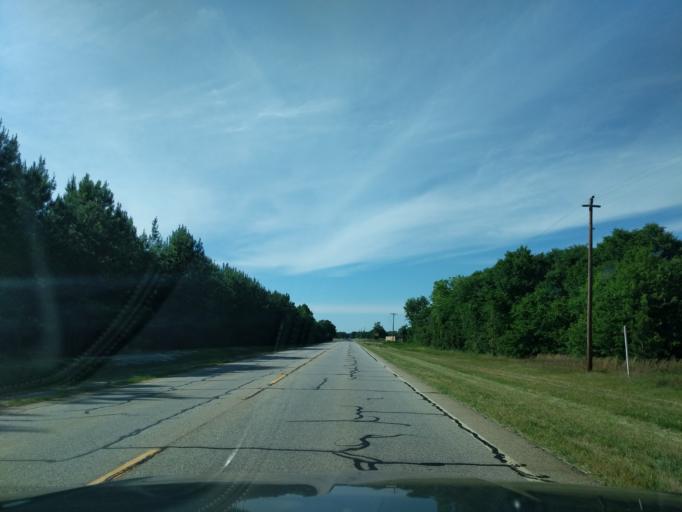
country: US
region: Georgia
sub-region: Jefferson County
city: Wrens
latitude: 33.2257
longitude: -82.3798
